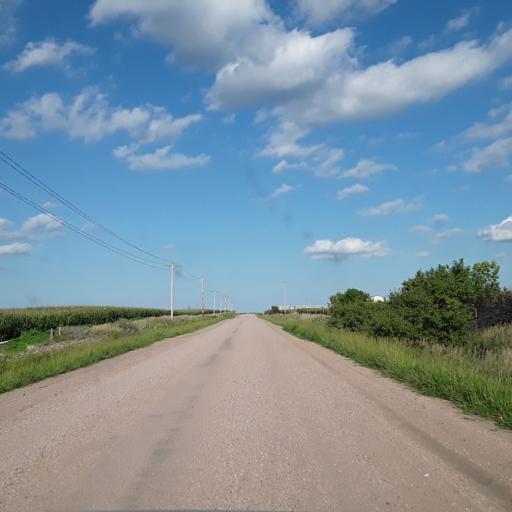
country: US
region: Nebraska
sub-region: Hall County
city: Wood River
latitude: 40.9169
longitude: -98.6037
